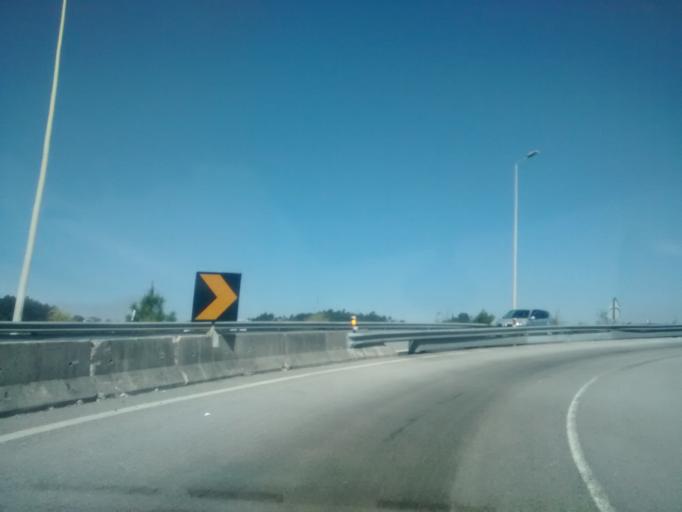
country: PT
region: Braga
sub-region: Braga
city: Braga
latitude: 41.5165
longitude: -8.4457
